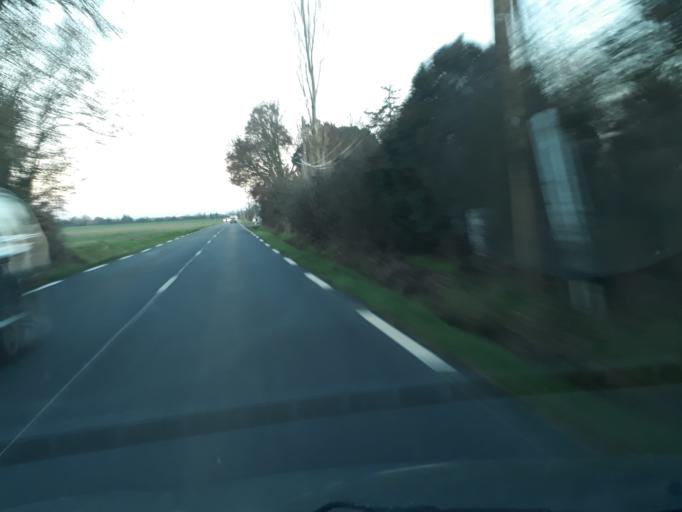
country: FR
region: Midi-Pyrenees
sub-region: Departement de la Haute-Garonne
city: Saint-Lys
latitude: 43.5380
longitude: 1.1642
